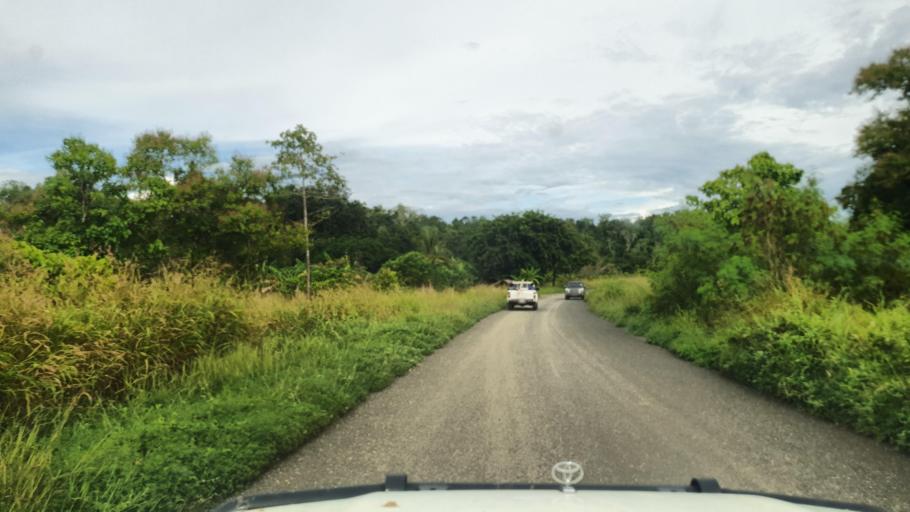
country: PG
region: Gulf
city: Kerema
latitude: -8.3384
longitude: 146.3278
